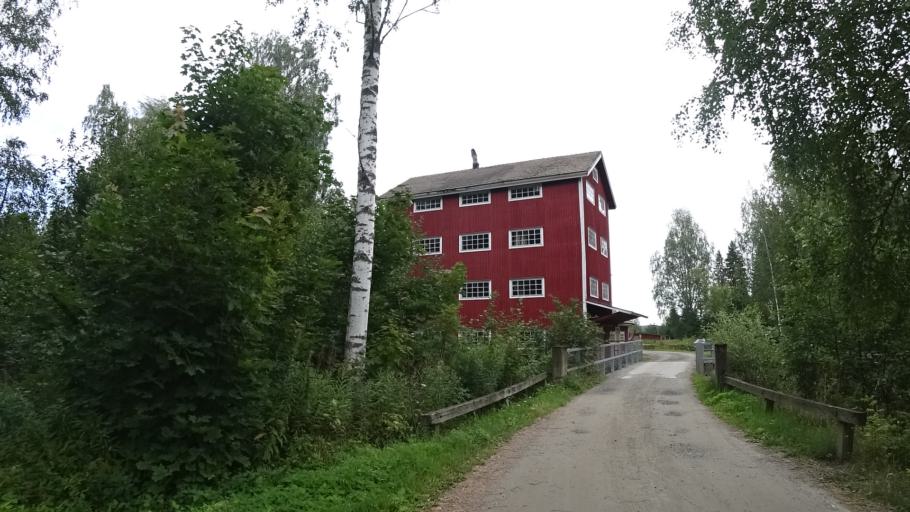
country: FI
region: North Karelia
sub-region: Keski-Karjala
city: Kesaelahti
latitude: 62.0945
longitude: 29.8737
